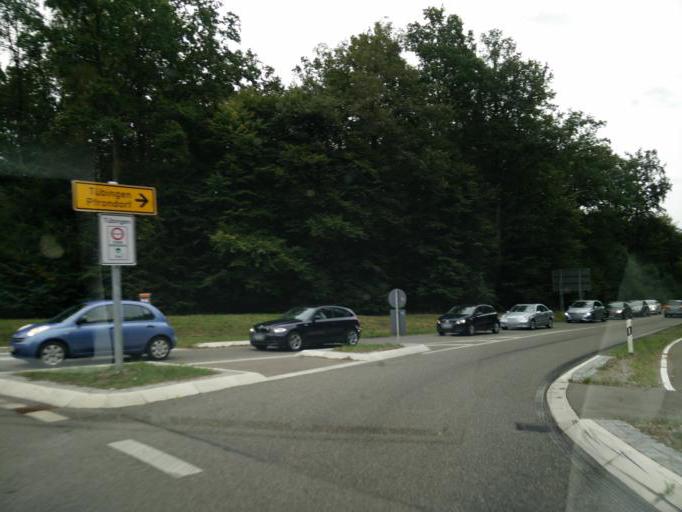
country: DE
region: Baden-Wuerttemberg
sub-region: Tuebingen Region
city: Dettenhausen
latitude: 48.5920
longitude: 9.1067
